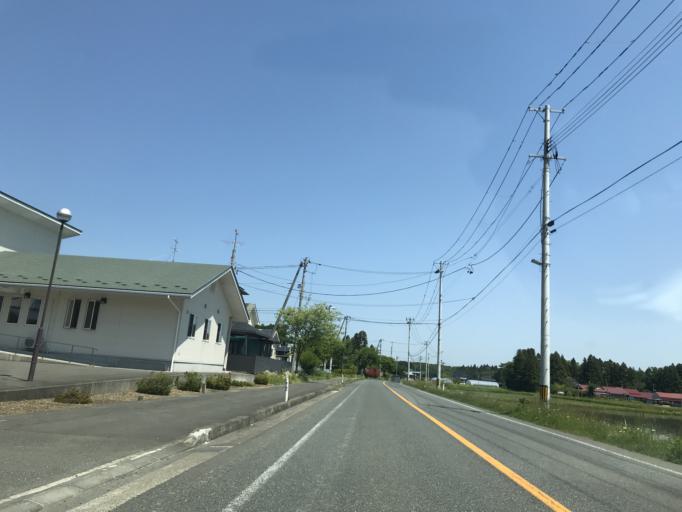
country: JP
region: Iwate
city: Kitakami
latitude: 39.2219
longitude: 141.0660
